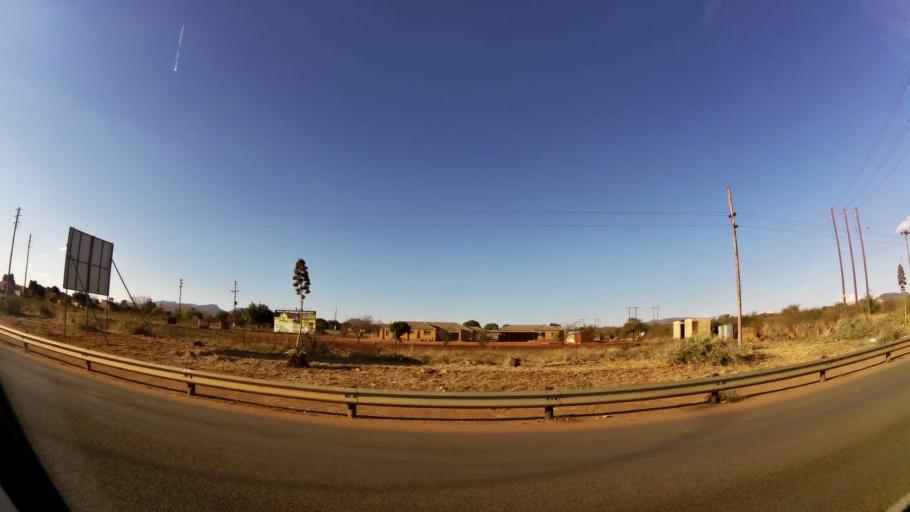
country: ZA
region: Limpopo
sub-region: Waterberg District Municipality
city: Mokopane
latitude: -24.1607
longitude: 28.9897
